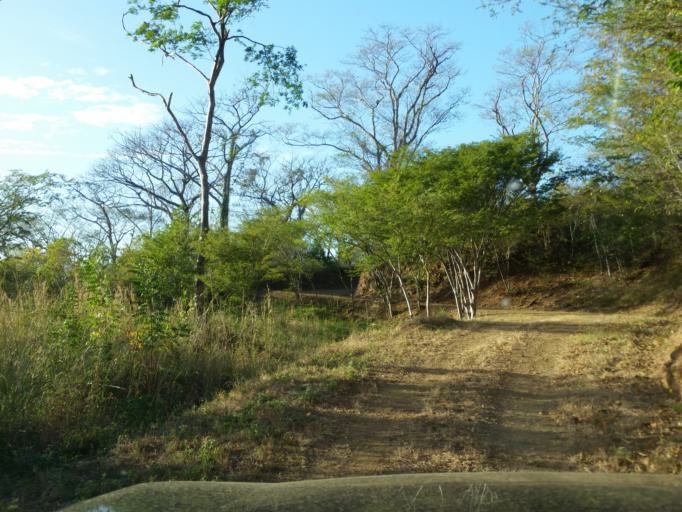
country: NI
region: Rivas
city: San Juan del Sur
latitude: 11.1817
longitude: -85.8121
